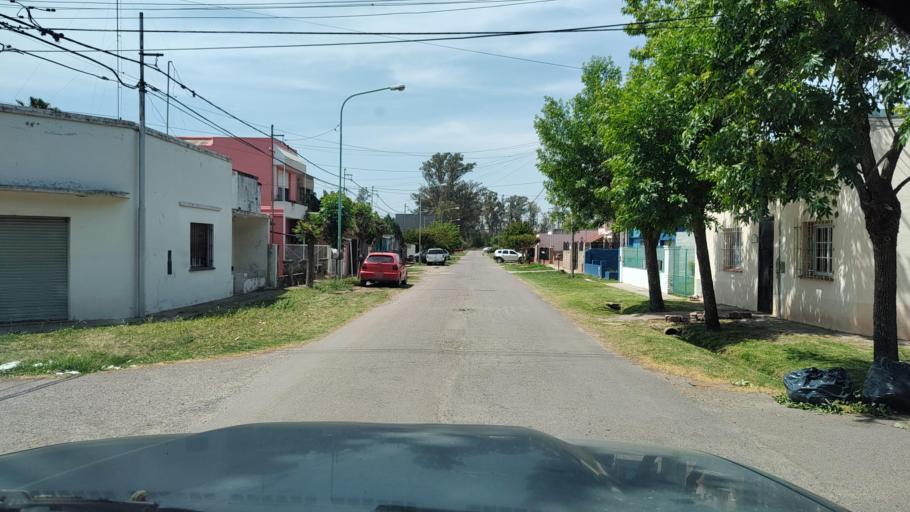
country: AR
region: Buenos Aires
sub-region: Partido de Lujan
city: Lujan
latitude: -34.6018
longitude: -59.1721
